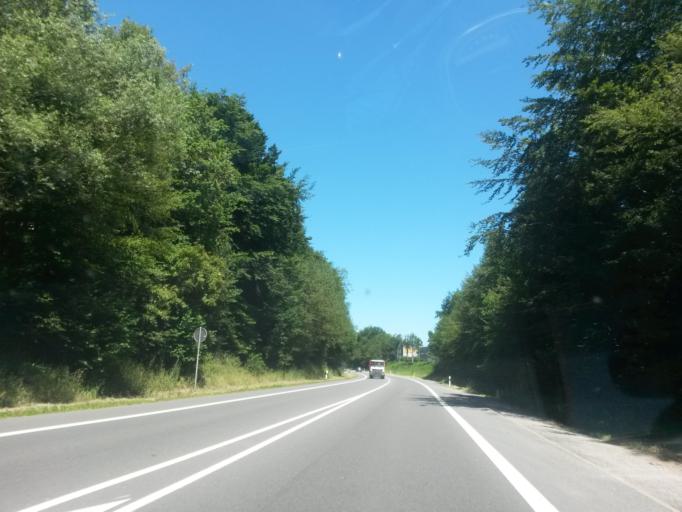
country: DE
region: North Rhine-Westphalia
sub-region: Regierungsbezirk Arnsberg
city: Luedenscheid
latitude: 51.2514
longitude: 7.5998
